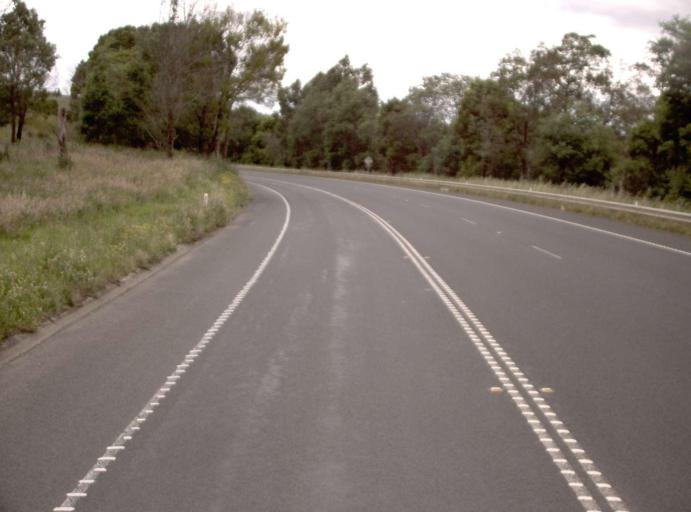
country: AU
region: Victoria
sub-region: Bass Coast
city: North Wonthaggi
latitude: -38.4260
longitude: 145.8030
